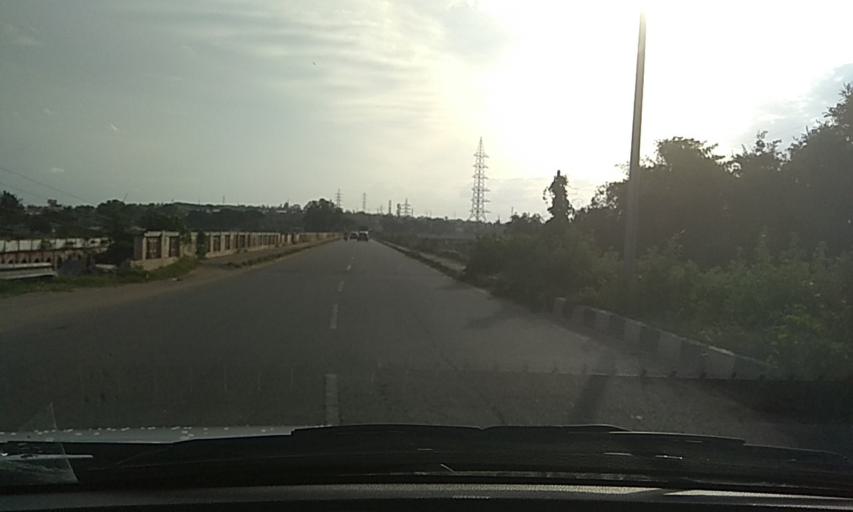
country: IN
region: Karnataka
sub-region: Mysore
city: Nanjangud
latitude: 12.1415
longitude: 76.6767
